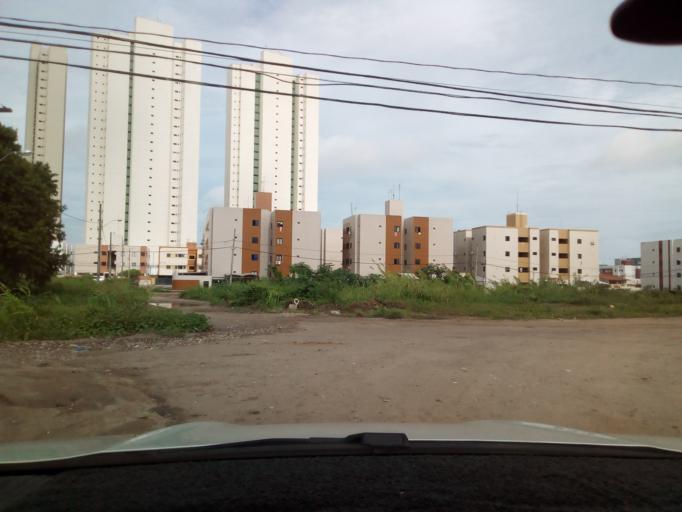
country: BR
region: Paraiba
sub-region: Joao Pessoa
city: Joao Pessoa
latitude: -7.1529
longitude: -34.8532
